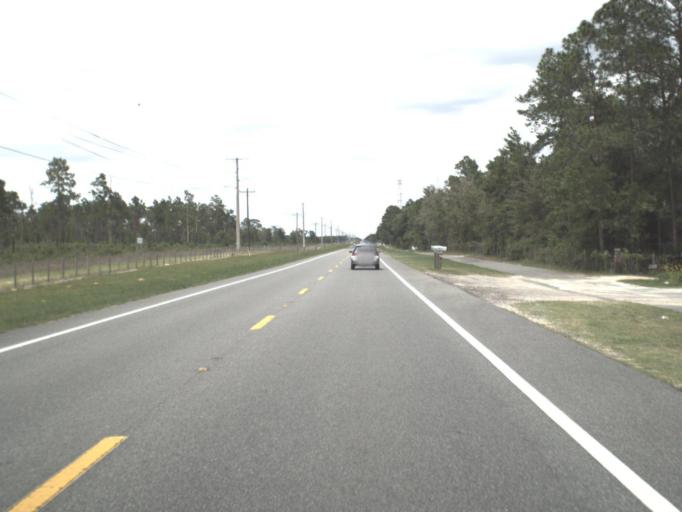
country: US
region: Florida
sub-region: Clay County
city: Keystone Heights
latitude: 29.8253
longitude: -81.9896
